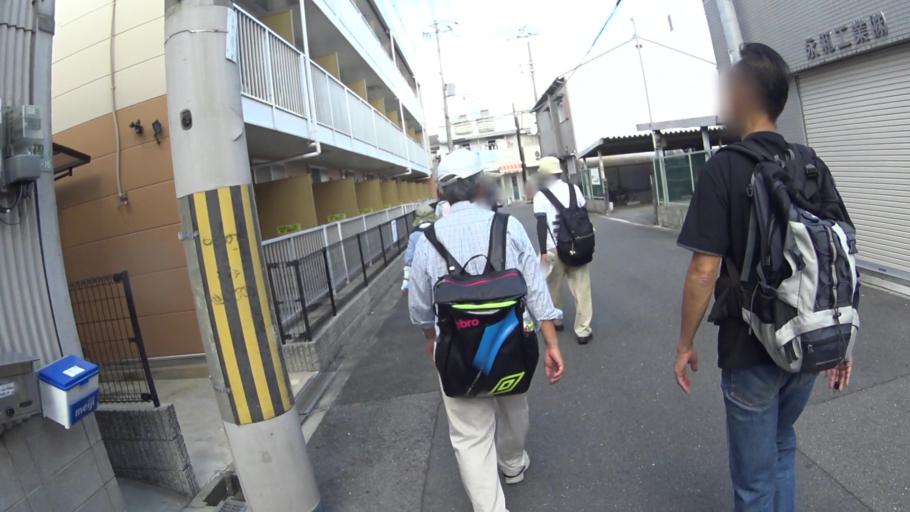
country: JP
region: Osaka
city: Yao
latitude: 34.6437
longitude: 135.5463
